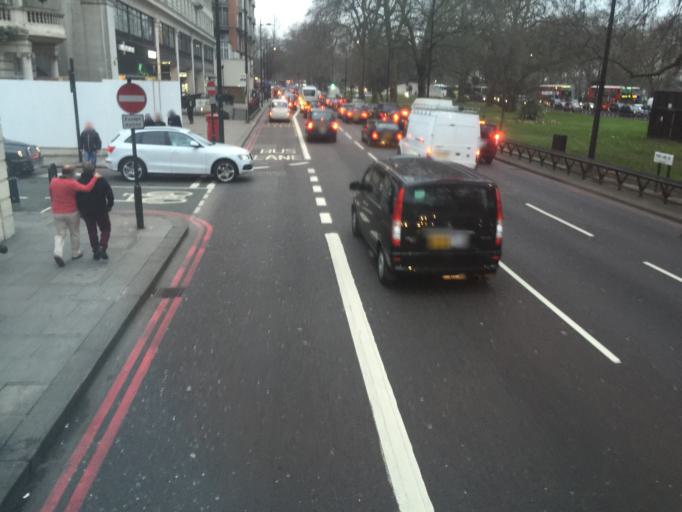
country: GB
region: England
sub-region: Greater London
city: Bayswater
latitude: 51.5124
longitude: -0.1577
